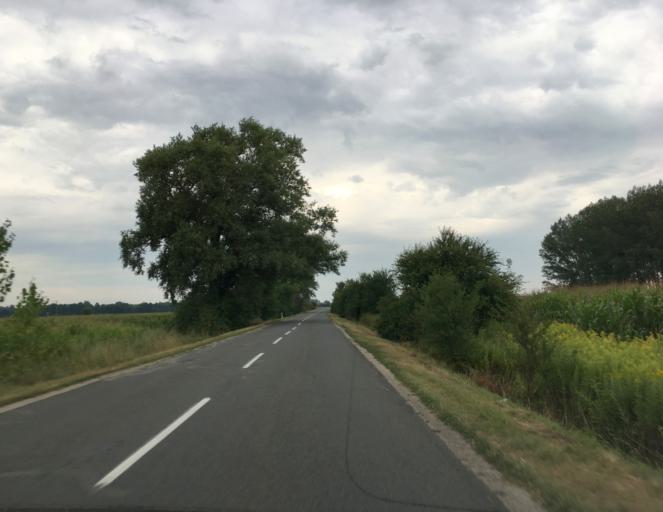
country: SK
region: Trnavsky
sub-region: Okres Dunajska Streda
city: Velky Meder
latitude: 47.8974
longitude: 17.6779
